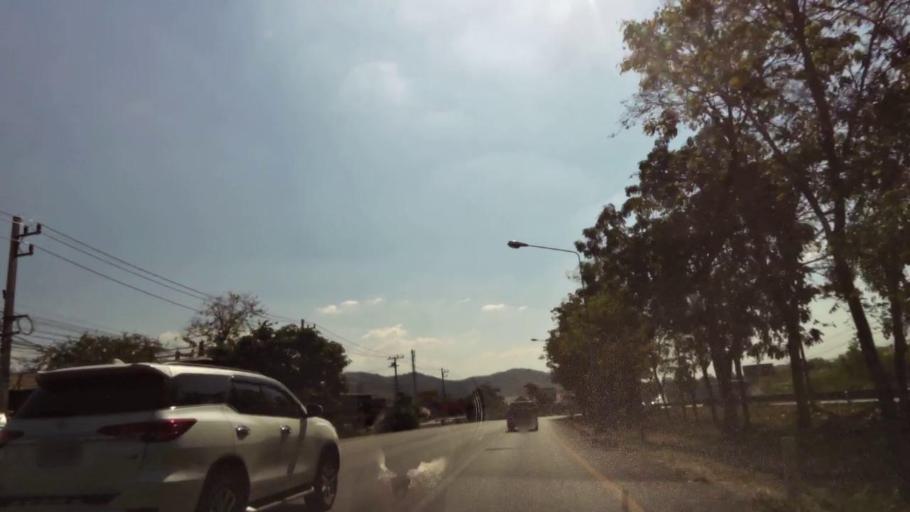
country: TH
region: Nakhon Sawan
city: Nakhon Sawan
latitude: 15.6428
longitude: 100.1346
